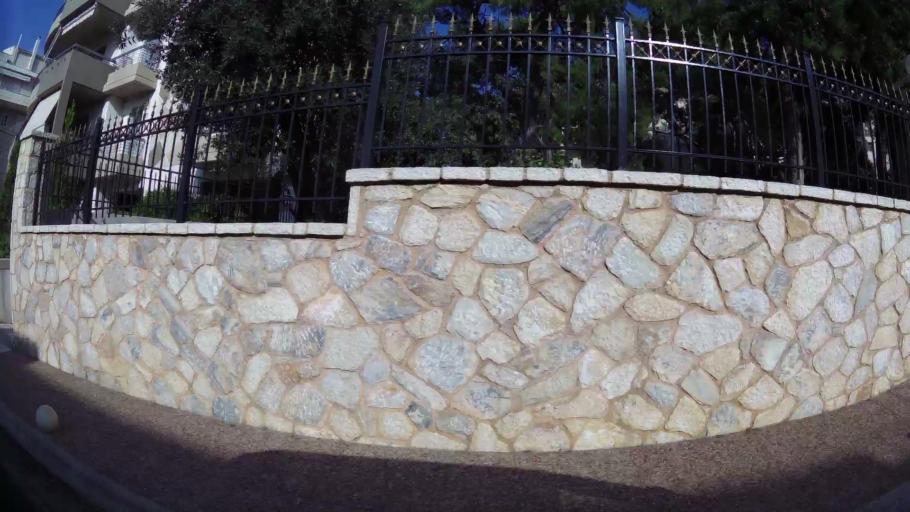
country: GR
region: Attica
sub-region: Nomarchia Athinas
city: Cholargos
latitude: 38.0085
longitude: 23.8091
